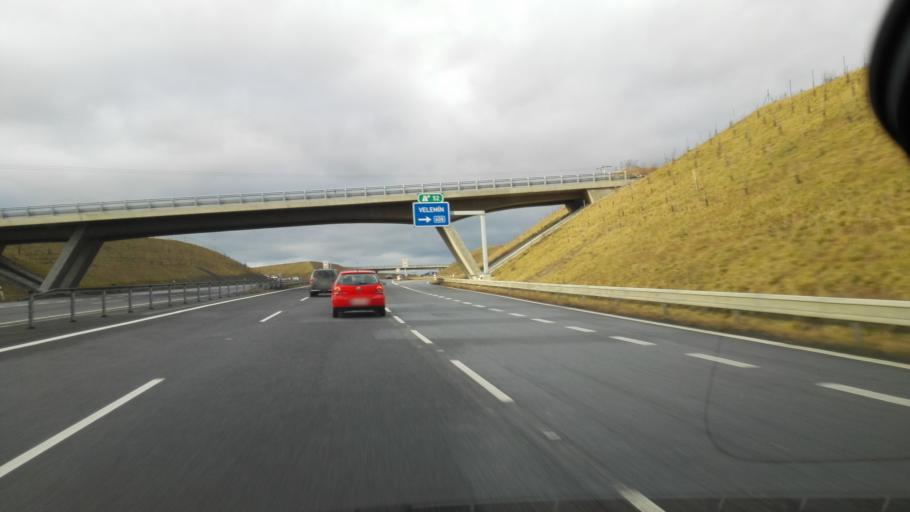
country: CZ
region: Ustecky
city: Velemin
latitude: 50.5244
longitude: 14.0030
